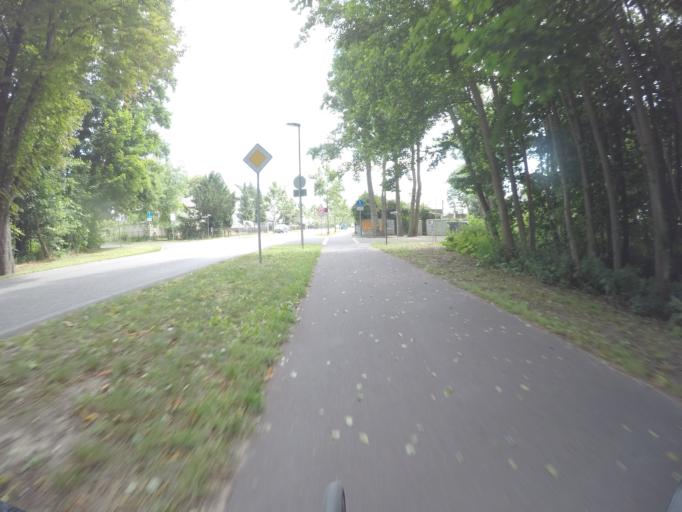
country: DE
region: Brandenburg
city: Storkow
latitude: 52.2511
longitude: 13.9392
